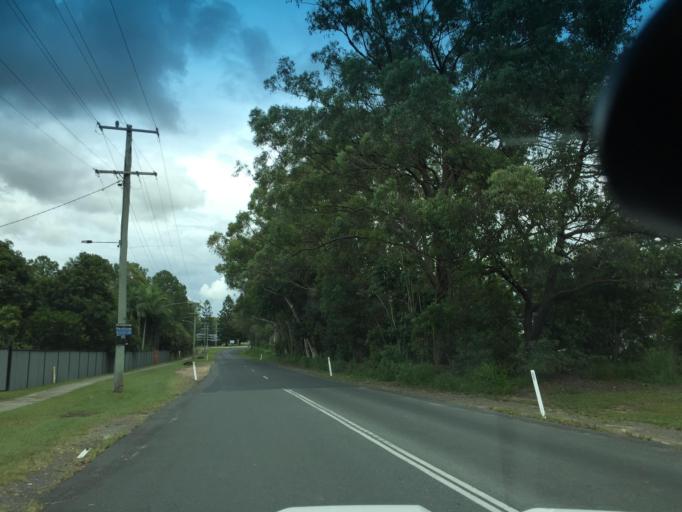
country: AU
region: Queensland
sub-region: Moreton Bay
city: Caboolture
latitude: -27.0446
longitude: 152.9343
